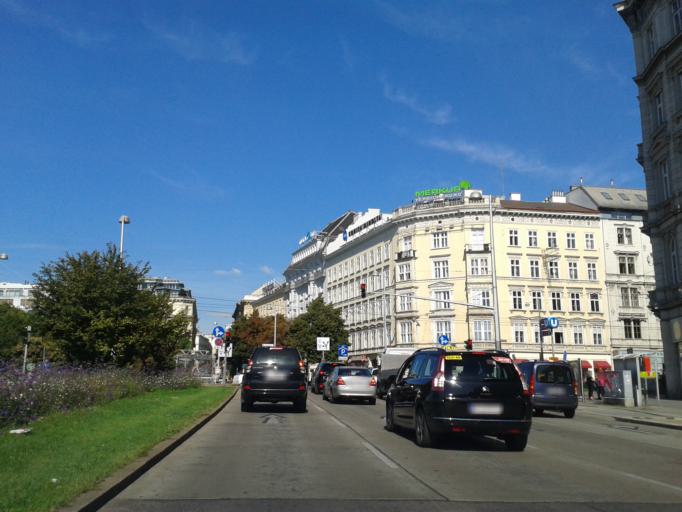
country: AT
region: Vienna
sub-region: Wien Stadt
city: Vienna
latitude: 48.2008
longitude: 16.3696
